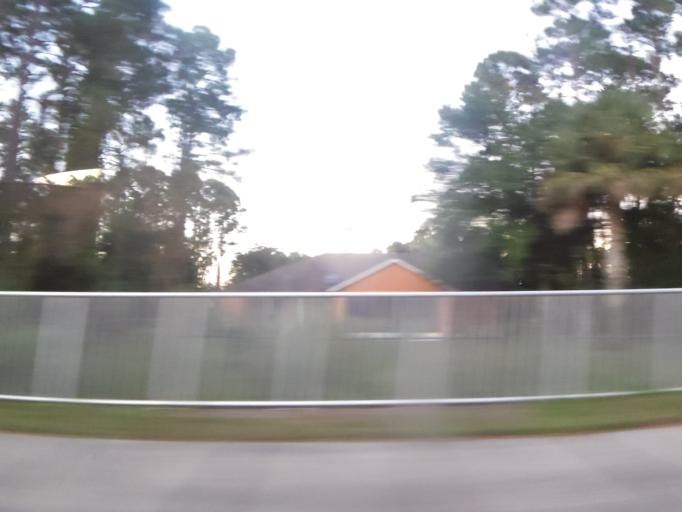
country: US
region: Florida
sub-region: Flagler County
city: Palm Coast
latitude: 29.5668
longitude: -81.2463
